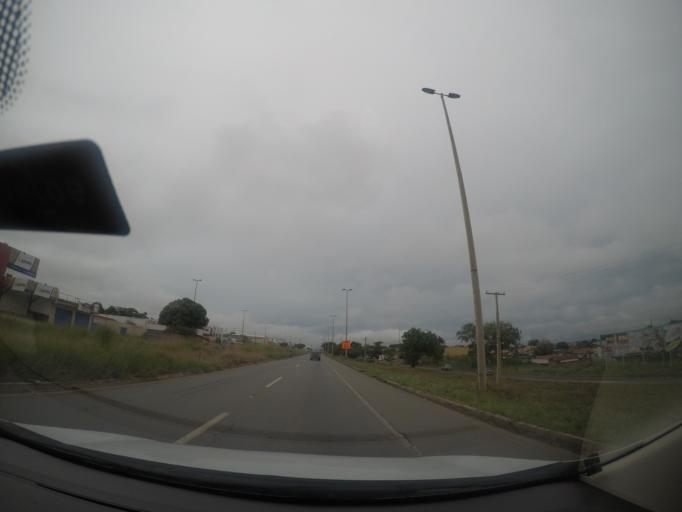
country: BR
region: Goias
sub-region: Aparecida De Goiania
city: Aparecida de Goiania
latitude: -16.7581
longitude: -49.3419
